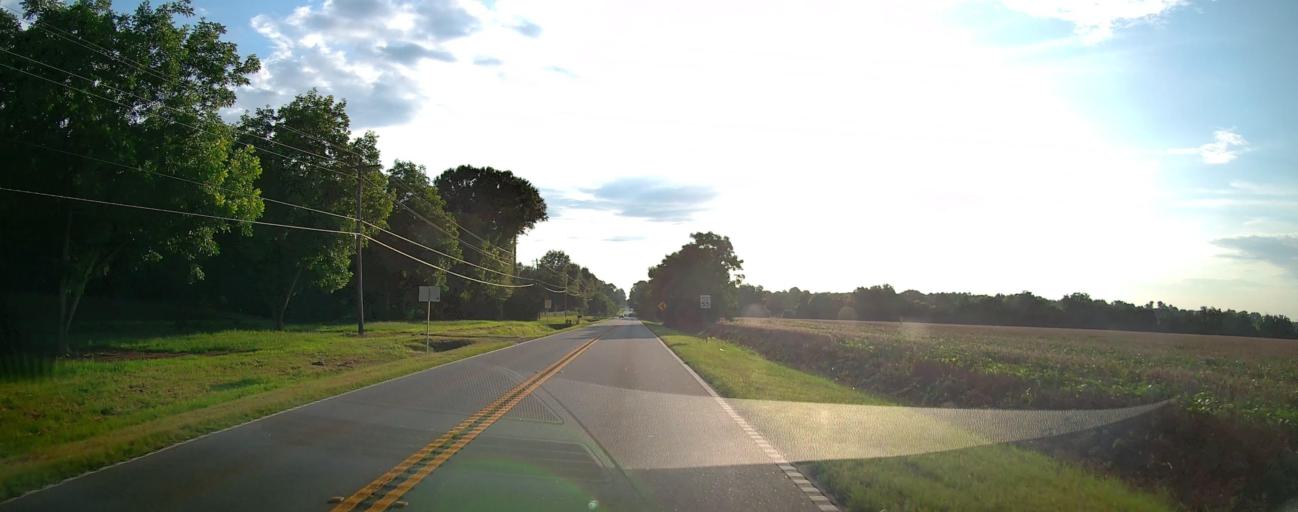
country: US
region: Georgia
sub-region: Peach County
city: Fort Valley
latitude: 32.5579
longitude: -83.9076
